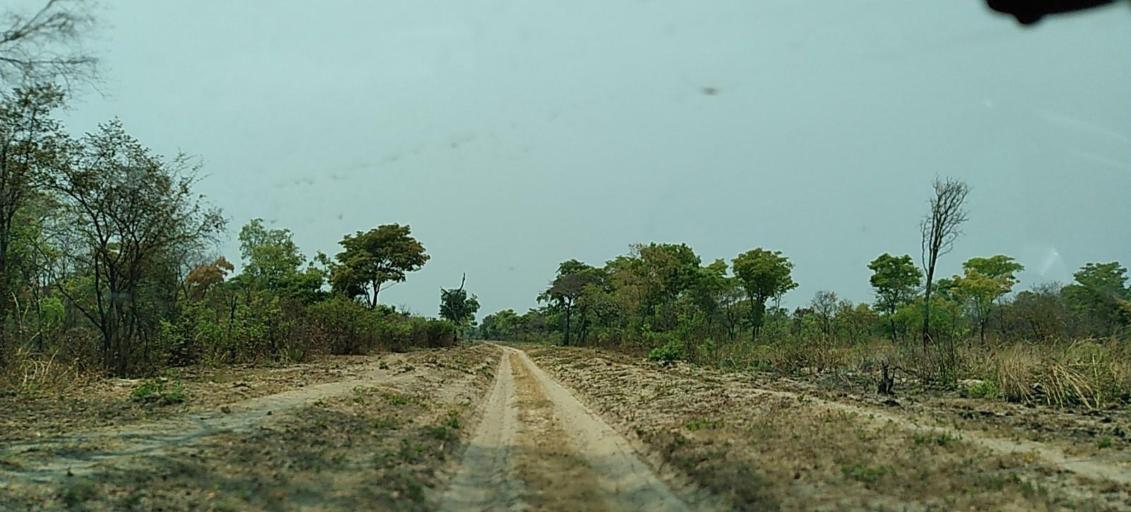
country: ZM
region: Western
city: Lukulu
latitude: -14.1464
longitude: 23.2897
